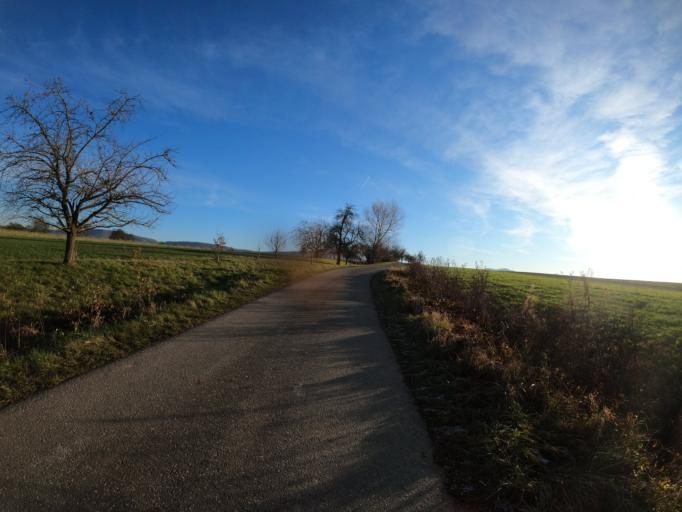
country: DE
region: Baden-Wuerttemberg
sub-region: Regierungsbezirk Stuttgart
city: Boll
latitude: 48.6573
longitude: 9.6090
